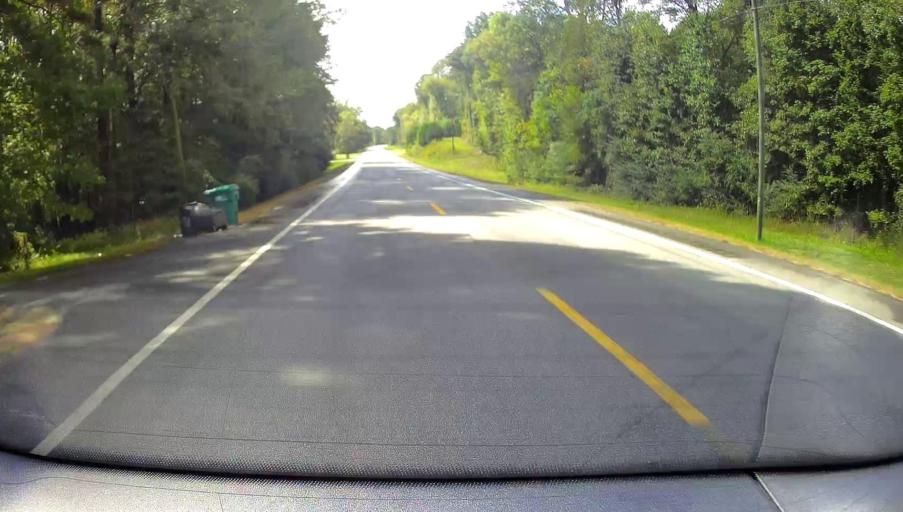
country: US
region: Georgia
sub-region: Baldwin County
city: Milledgeville
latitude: 33.0345
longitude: -83.3124
